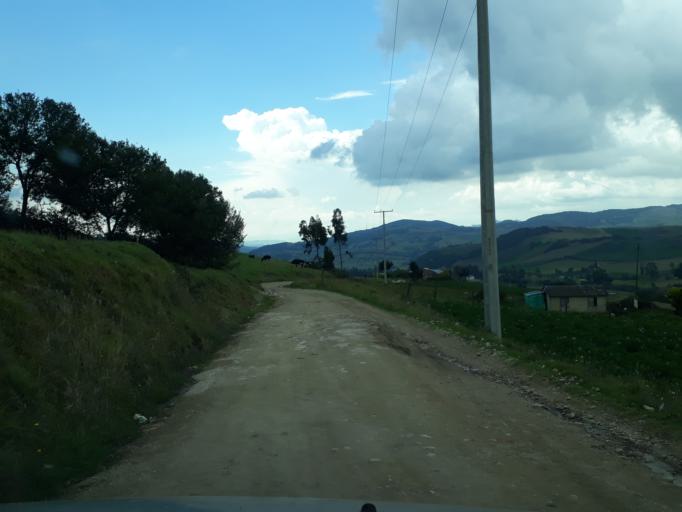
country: CO
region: Cundinamarca
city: Lenguazaque
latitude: 5.2417
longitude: -73.6755
